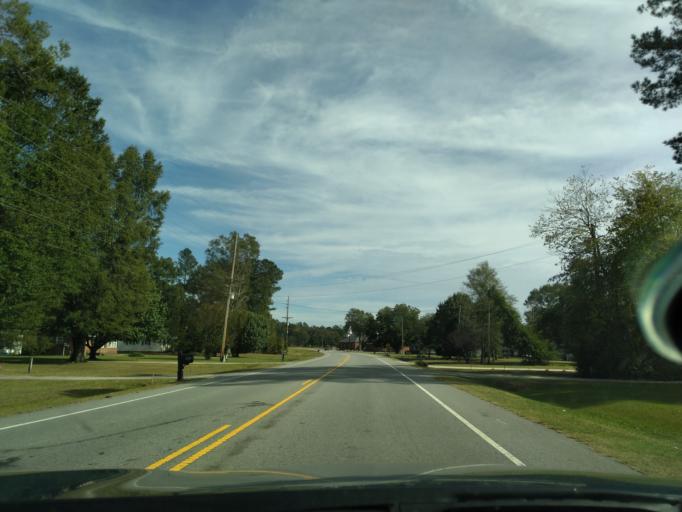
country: US
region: North Carolina
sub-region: Beaufort County
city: River Road
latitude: 35.5138
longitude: -76.9124
